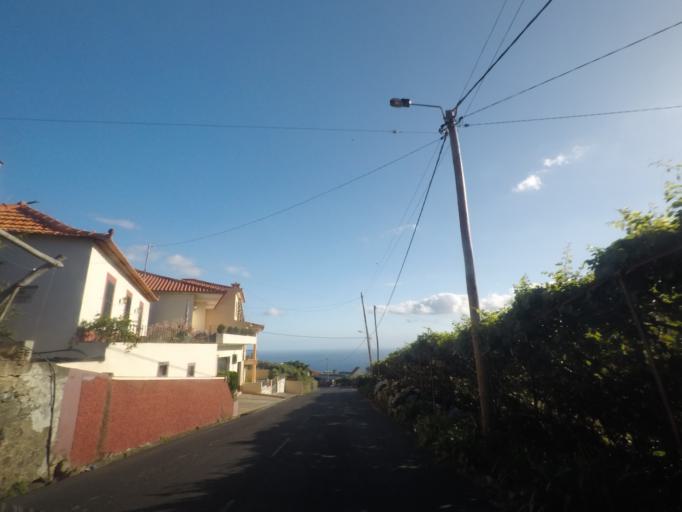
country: PT
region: Madeira
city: Camara de Lobos
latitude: 32.6672
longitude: -16.9798
